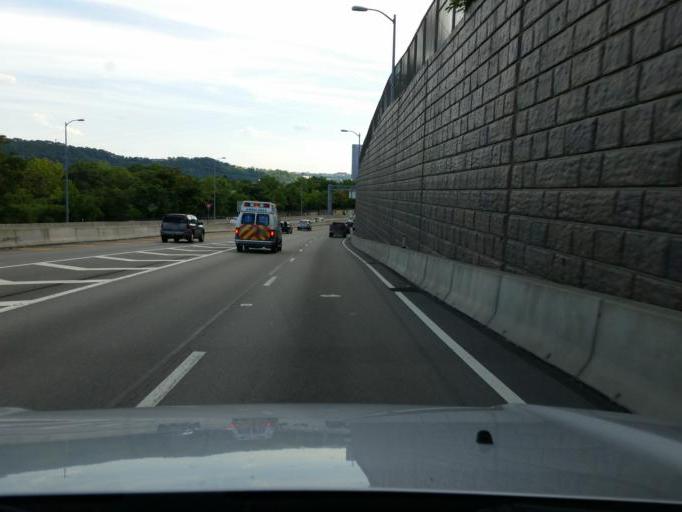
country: US
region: Pennsylvania
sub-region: Allegheny County
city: Millvale
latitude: 40.4734
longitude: -79.9724
